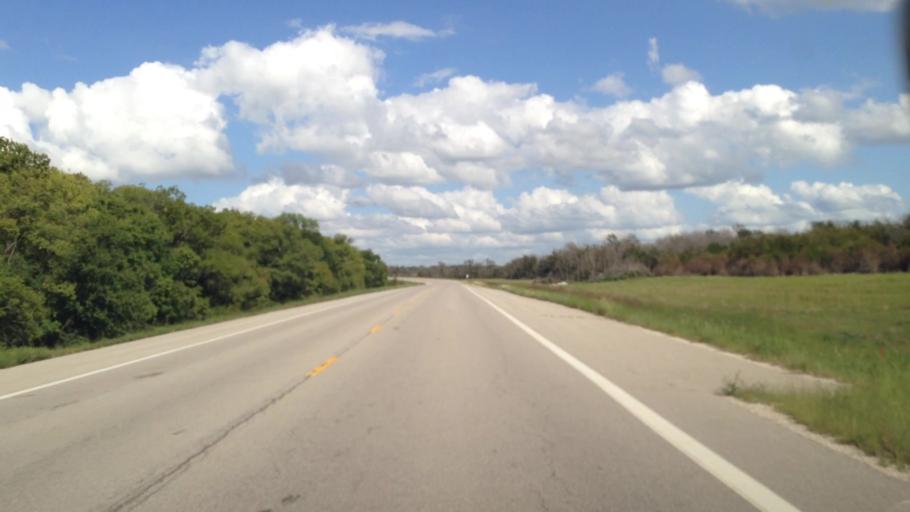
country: US
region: Kansas
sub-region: Neosho County
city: Erie
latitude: 37.6888
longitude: -95.1698
